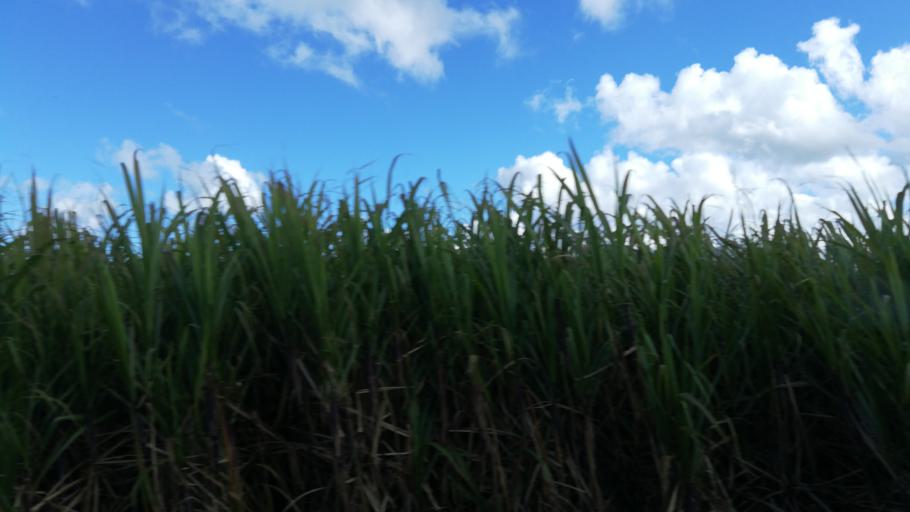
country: MU
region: Moka
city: Quartier Militaire
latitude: -20.2293
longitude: 57.5758
